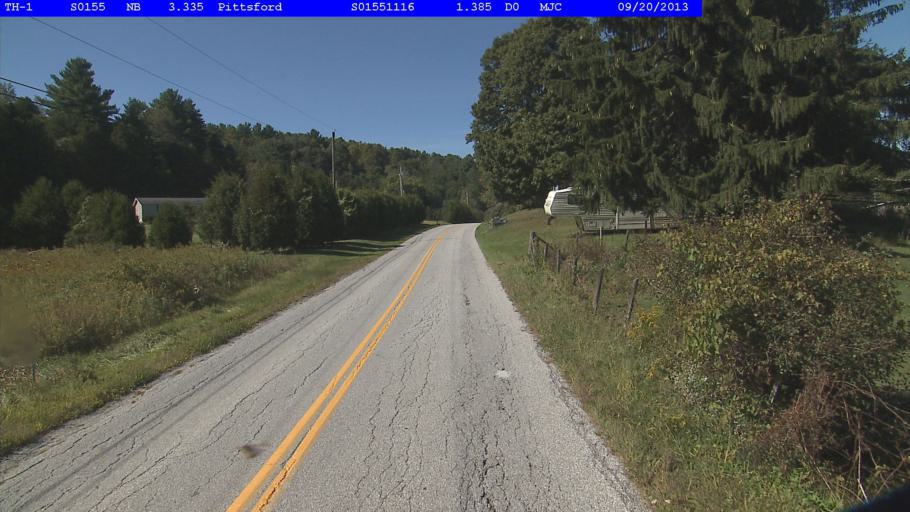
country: US
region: Vermont
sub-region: Rutland County
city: Brandon
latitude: 43.7089
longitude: -73.0547
